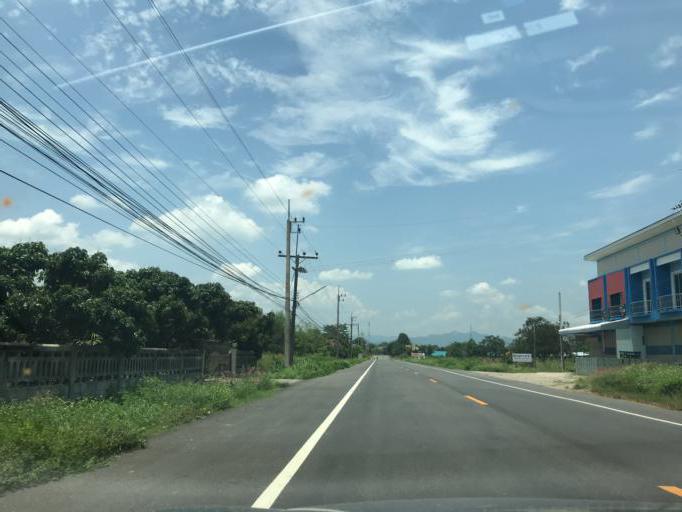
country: TH
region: Phayao
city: Phu Sang
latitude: 19.5903
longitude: 100.3135
